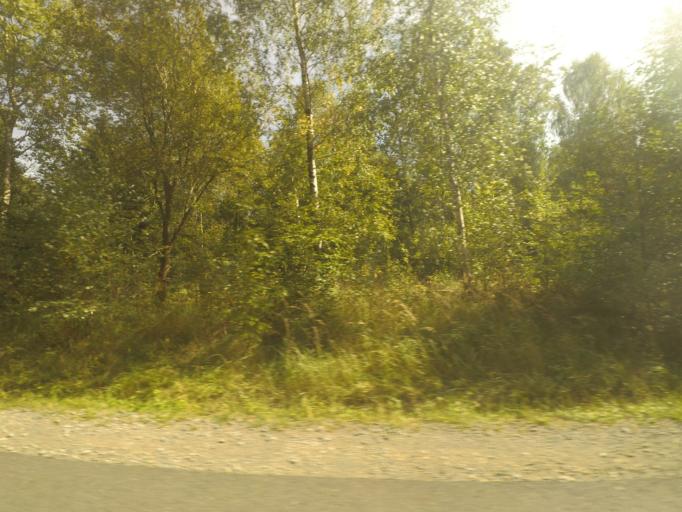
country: DE
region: Thuringia
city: Christes
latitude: 50.6471
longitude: 10.4665
